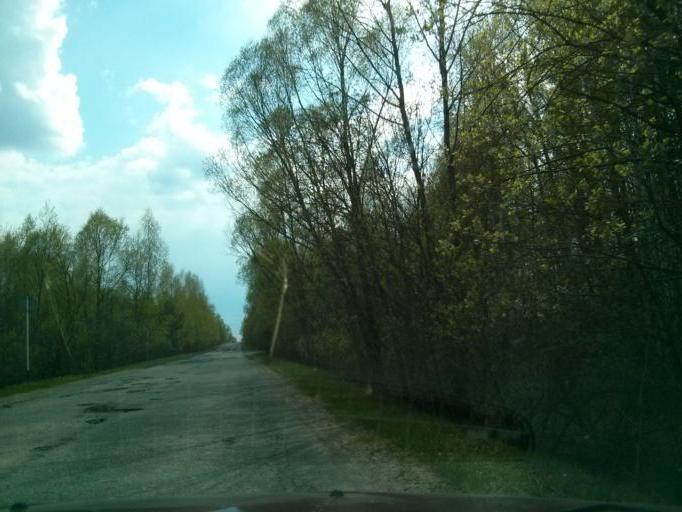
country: RU
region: Nizjnij Novgorod
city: Shimorskoye
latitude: 55.4496
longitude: 41.9802
